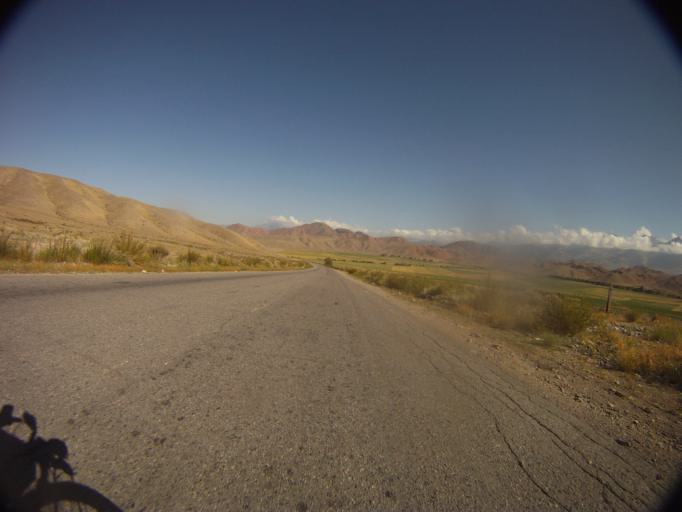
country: KG
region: Ysyk-Koel
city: Bokombayevskoye
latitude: 42.1358
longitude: 76.7768
